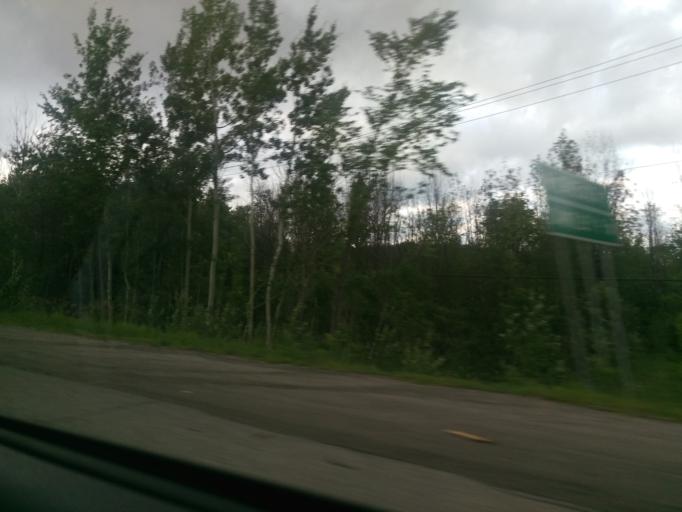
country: CA
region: Quebec
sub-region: Outaouais
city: Gatineau
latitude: 45.4815
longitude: -75.7478
